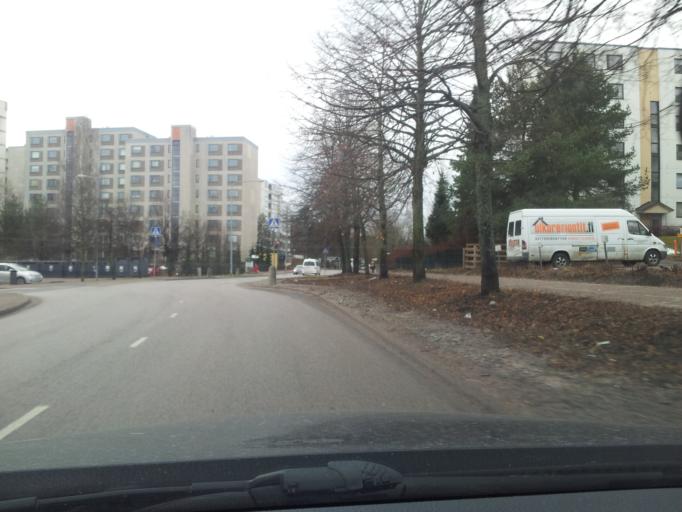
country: FI
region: Uusimaa
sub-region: Helsinki
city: Espoo
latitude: 60.2019
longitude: 24.6683
